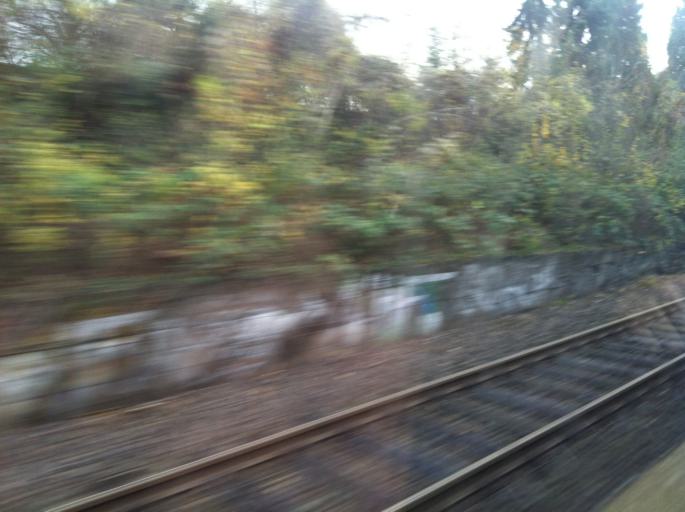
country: DE
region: North Rhine-Westphalia
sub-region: Regierungsbezirk Koln
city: Poll
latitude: 50.8976
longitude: 6.9863
